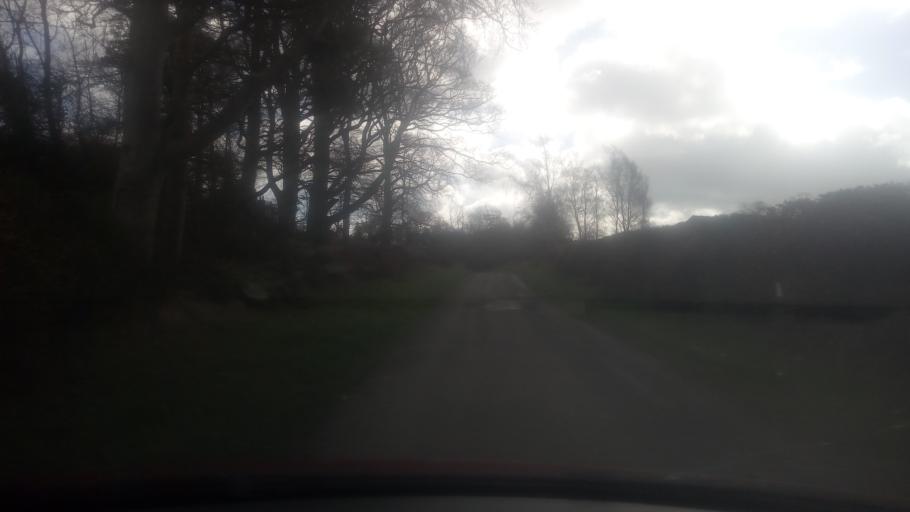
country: GB
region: Scotland
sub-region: The Scottish Borders
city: Saint Boswells
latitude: 55.5505
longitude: -2.5919
